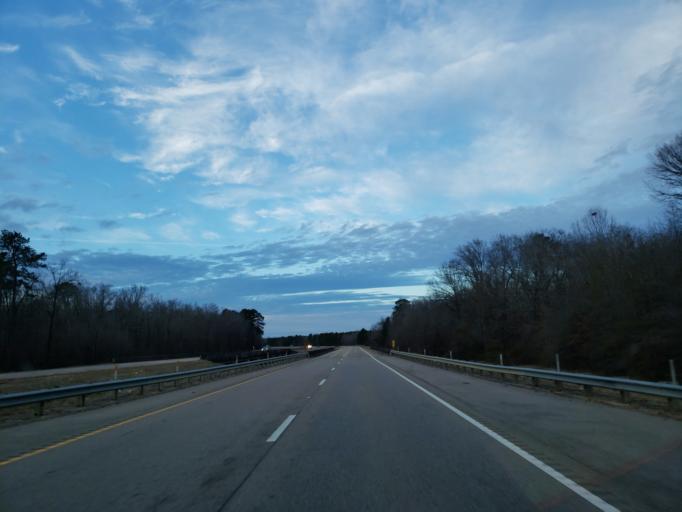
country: US
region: Mississippi
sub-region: Kemper County
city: De Kalb
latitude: 32.7980
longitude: -88.4554
